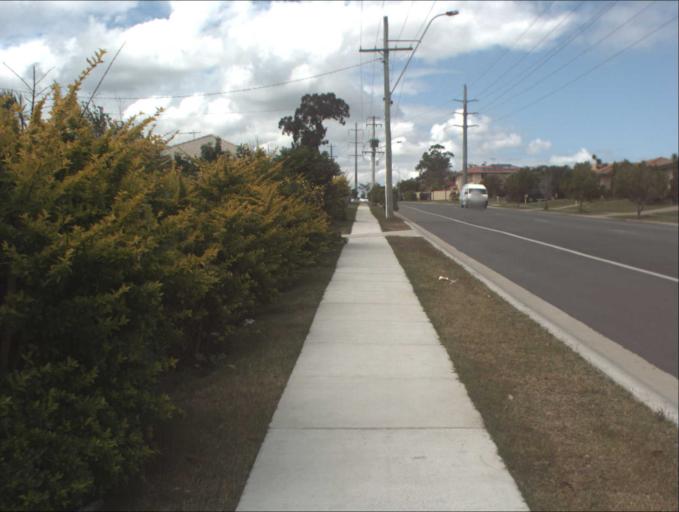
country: AU
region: Queensland
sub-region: Logan
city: Woodridge
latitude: -27.6696
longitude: 153.0826
